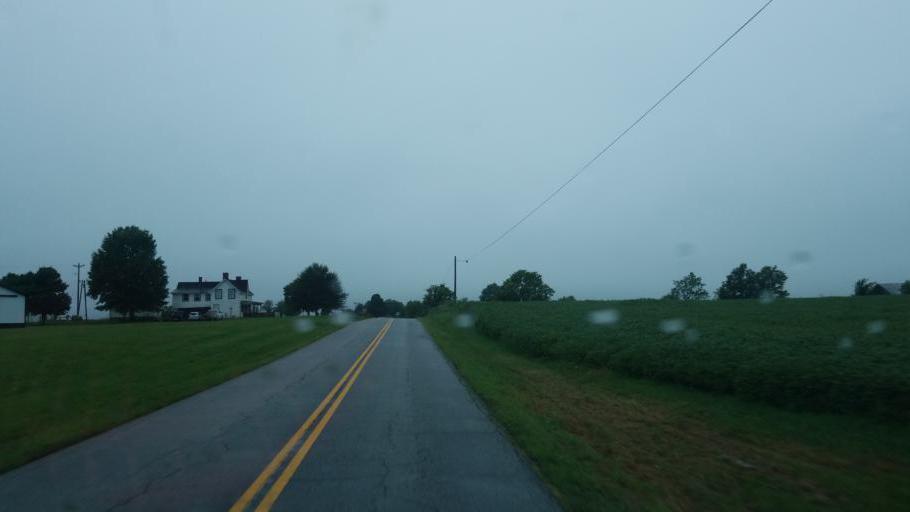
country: US
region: Kentucky
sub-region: Fleming County
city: Flemingsburg
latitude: 38.4141
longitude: -83.6680
